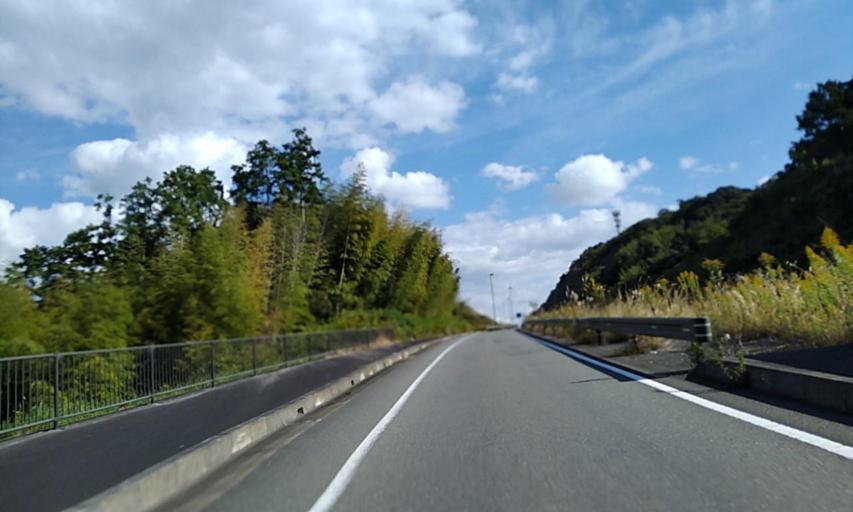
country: JP
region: Wakayama
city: Tanabe
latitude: 33.7514
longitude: 135.3554
